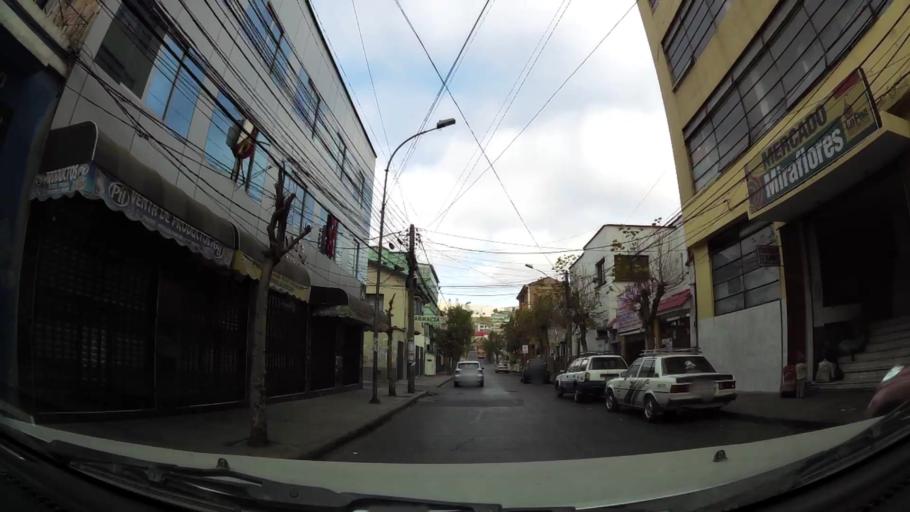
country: BO
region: La Paz
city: La Paz
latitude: -16.5016
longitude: -68.1218
